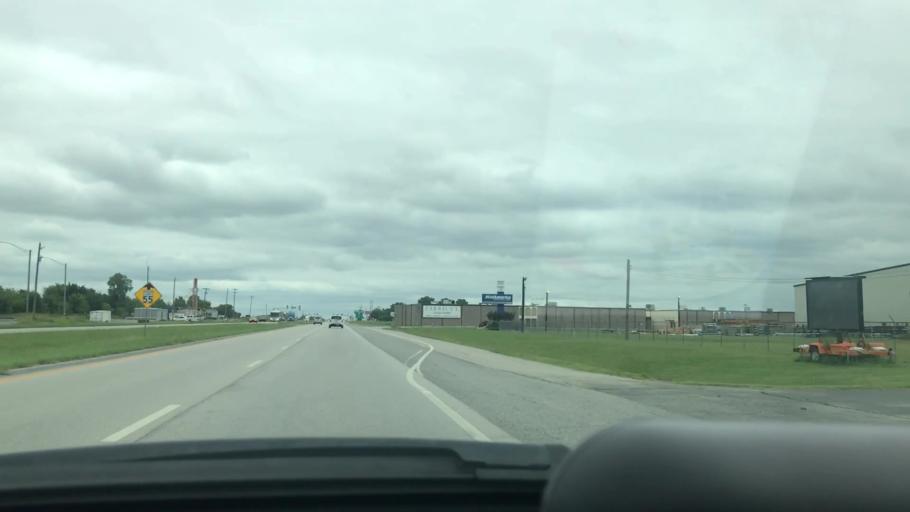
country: US
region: Oklahoma
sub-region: Mayes County
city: Chouteau
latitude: 36.2410
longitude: -95.3374
